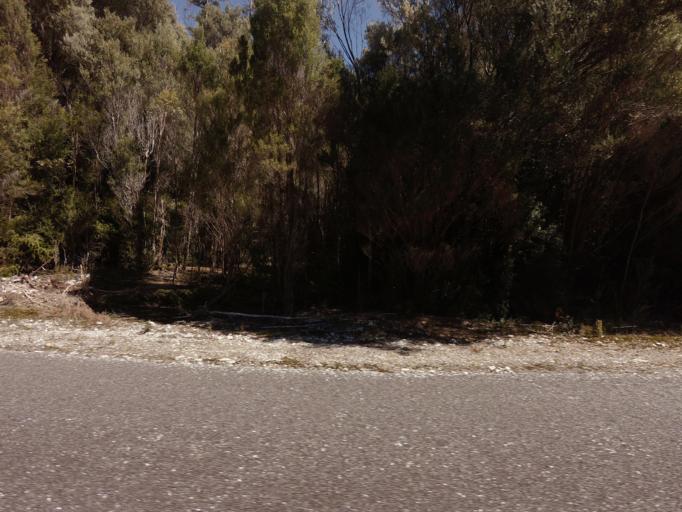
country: AU
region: Tasmania
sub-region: West Coast
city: Queenstown
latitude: -42.7680
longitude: 146.0059
